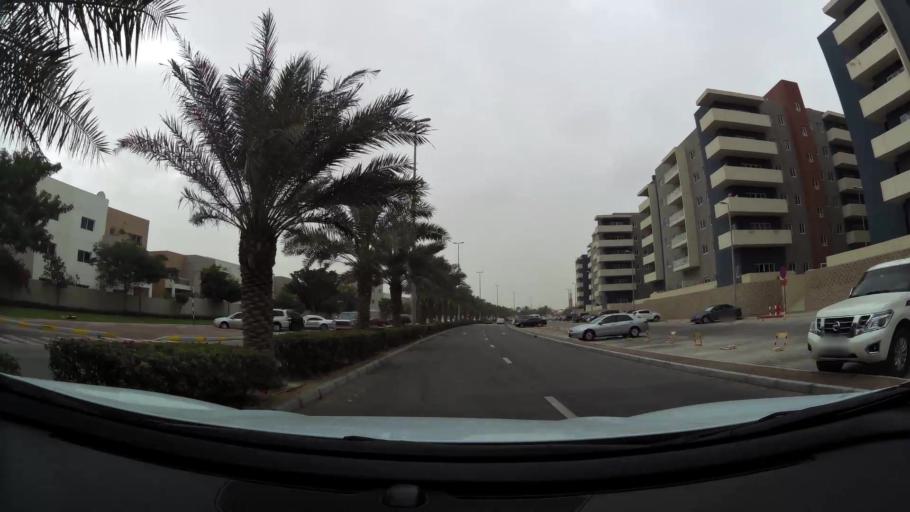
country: AE
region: Abu Dhabi
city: Abu Dhabi
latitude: 24.4564
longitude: 54.6744
